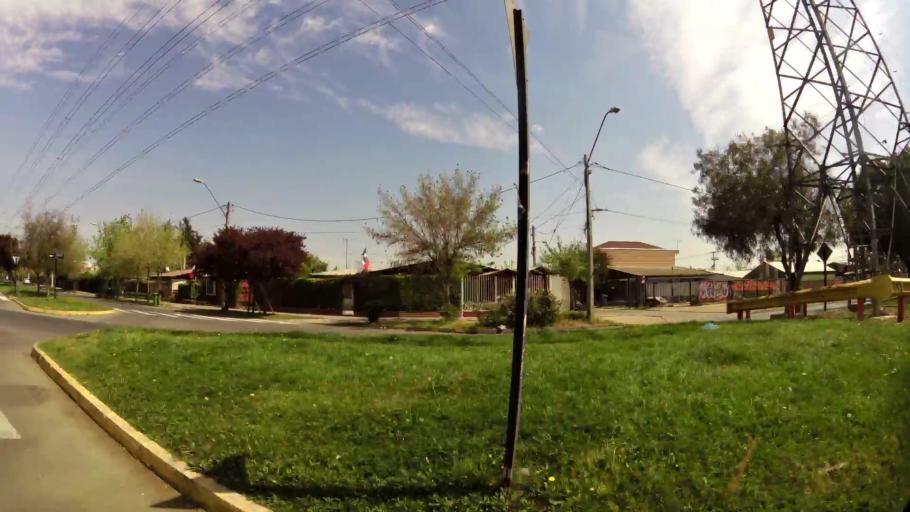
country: CL
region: Santiago Metropolitan
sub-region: Provincia de Cordillera
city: Puente Alto
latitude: -33.5882
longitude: -70.5965
